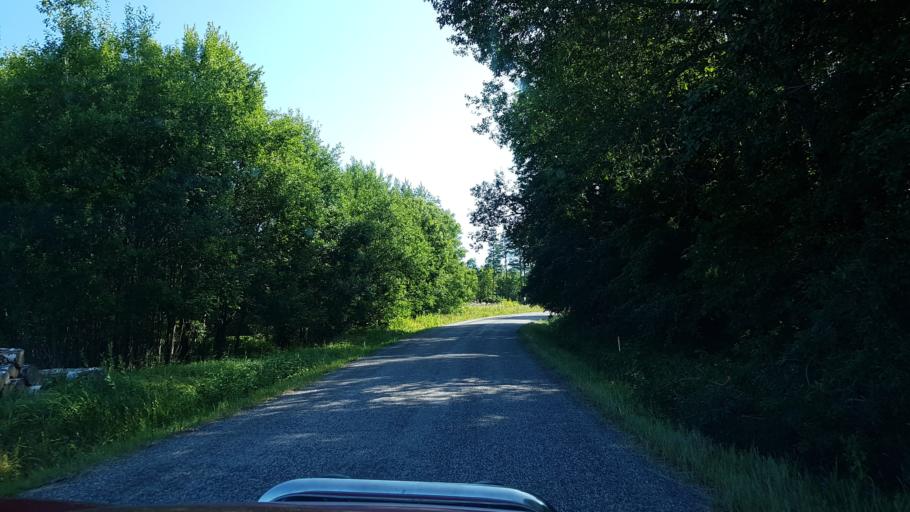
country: EE
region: Vorumaa
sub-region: Voru linn
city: Voru
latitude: 57.7096
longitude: 27.1774
